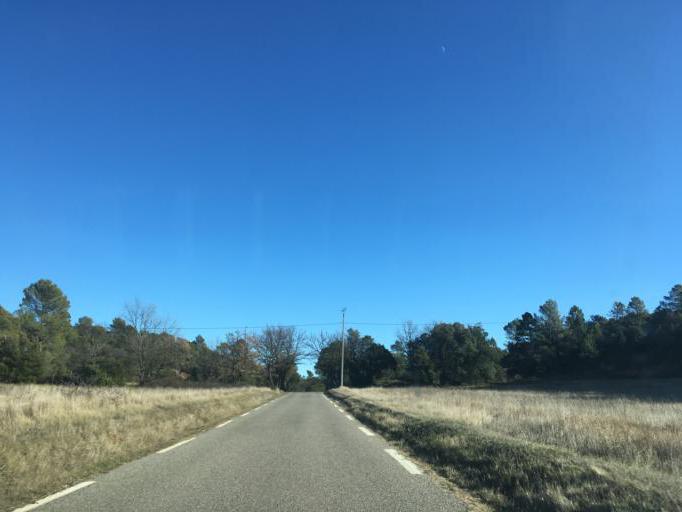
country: FR
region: Provence-Alpes-Cote d'Azur
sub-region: Departement du Var
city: Barjols
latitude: 43.5934
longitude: 6.0634
